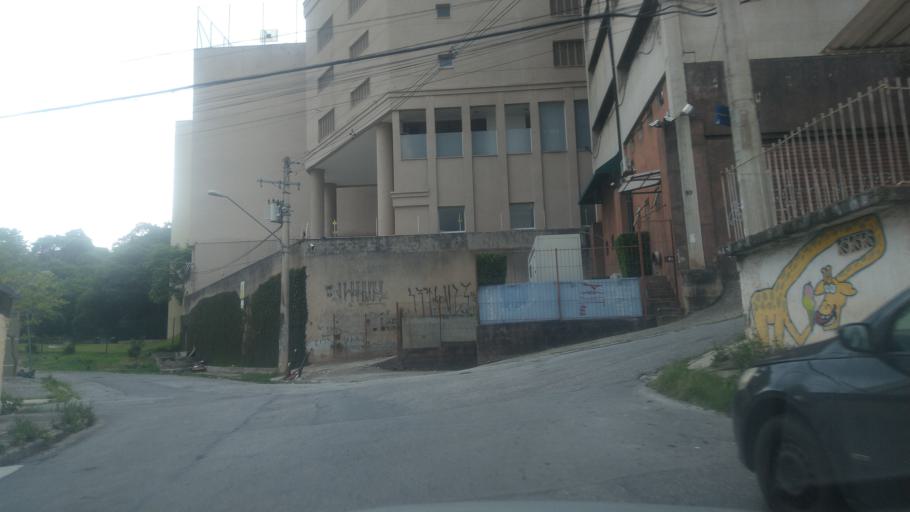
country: BR
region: Sao Paulo
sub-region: Sao Paulo
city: Sao Paulo
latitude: -23.4869
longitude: -46.6260
